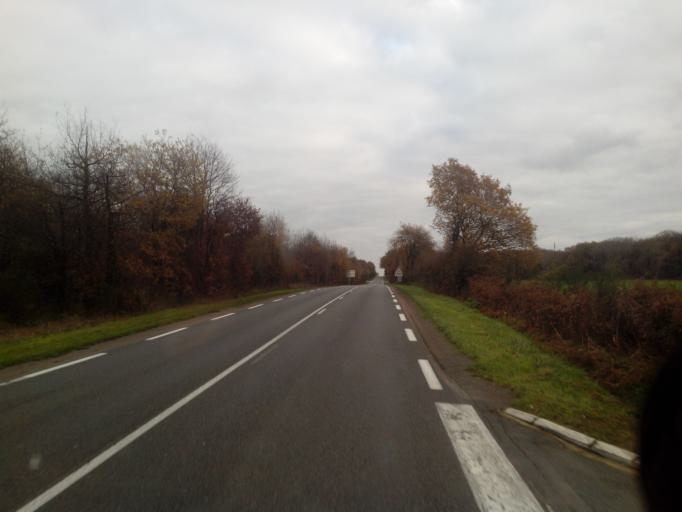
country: FR
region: Poitou-Charentes
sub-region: Departement des Deux-Sevres
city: Chiche
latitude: 46.8145
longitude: -0.3962
